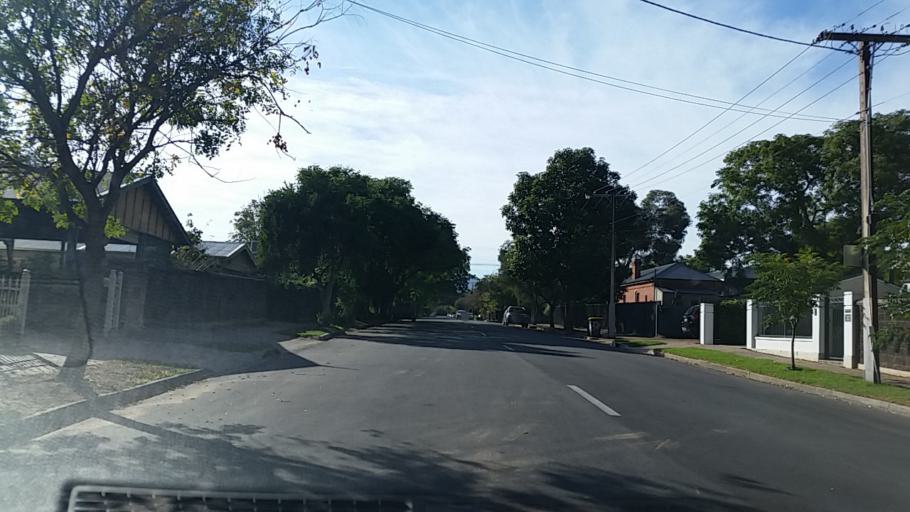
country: AU
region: South Australia
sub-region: Mitcham
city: Hawthorn
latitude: -34.9696
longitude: 138.6036
